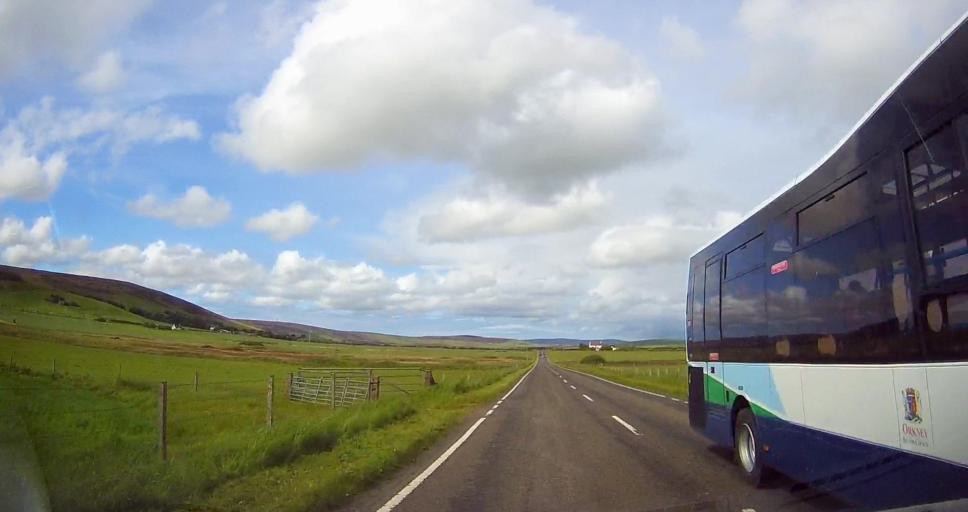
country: GB
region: Scotland
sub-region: Orkney Islands
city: Orkney
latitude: 59.0255
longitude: -3.0953
